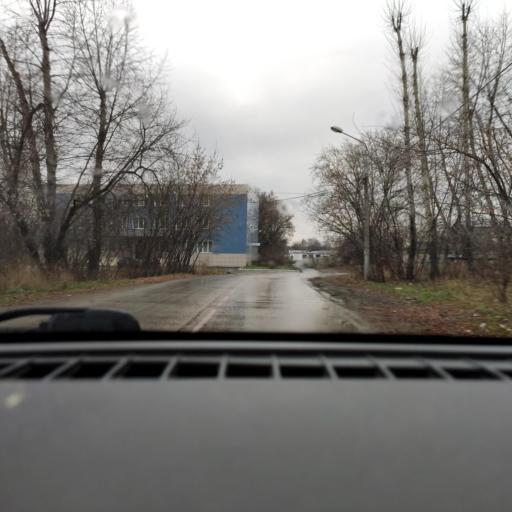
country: RU
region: Perm
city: Kultayevo
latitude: 57.9975
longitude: 55.9345
